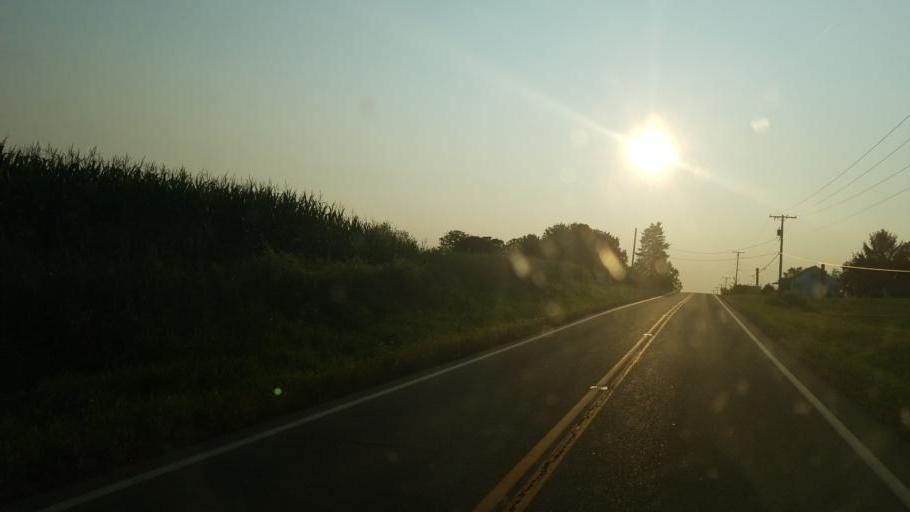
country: US
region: Ohio
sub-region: Wayne County
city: Shreve
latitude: 40.6684
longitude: -82.0675
